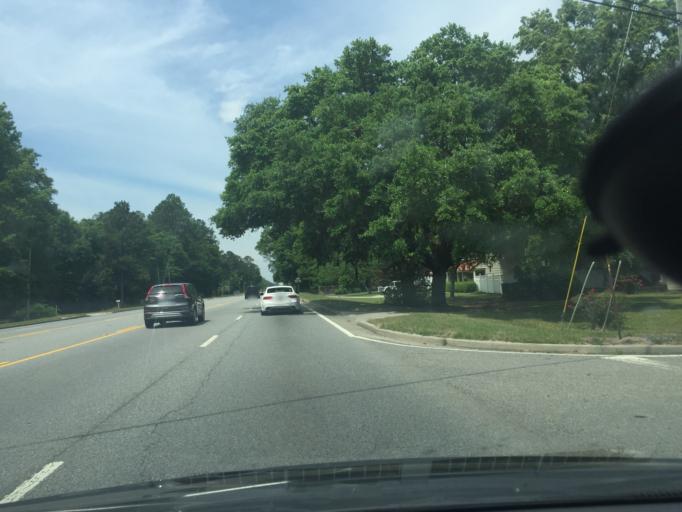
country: US
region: Georgia
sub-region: Chatham County
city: Bloomingdale
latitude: 32.1286
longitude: -81.2874
